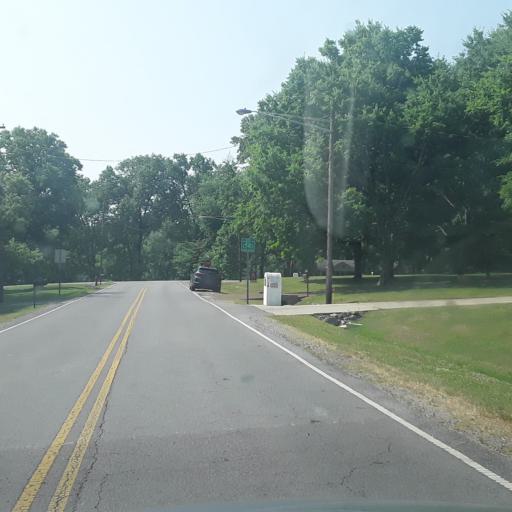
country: US
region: Tennessee
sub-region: Williamson County
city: Brentwood
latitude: 36.0517
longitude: -86.7589
